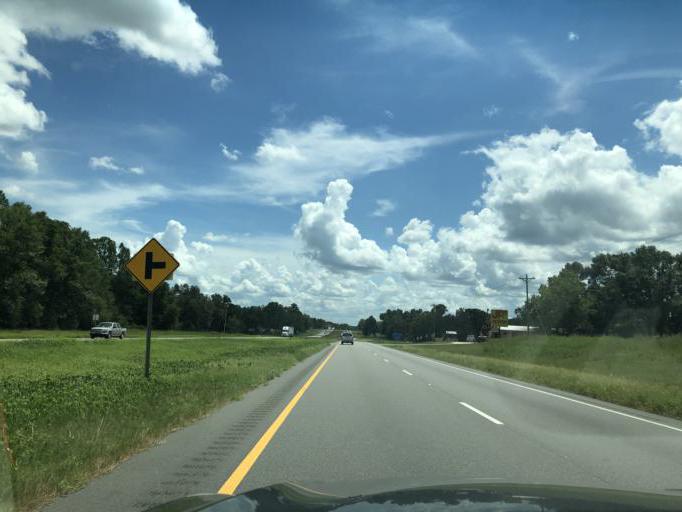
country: US
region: Alabama
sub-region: Houston County
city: Cottonwood
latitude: 31.0057
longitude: -85.4079
